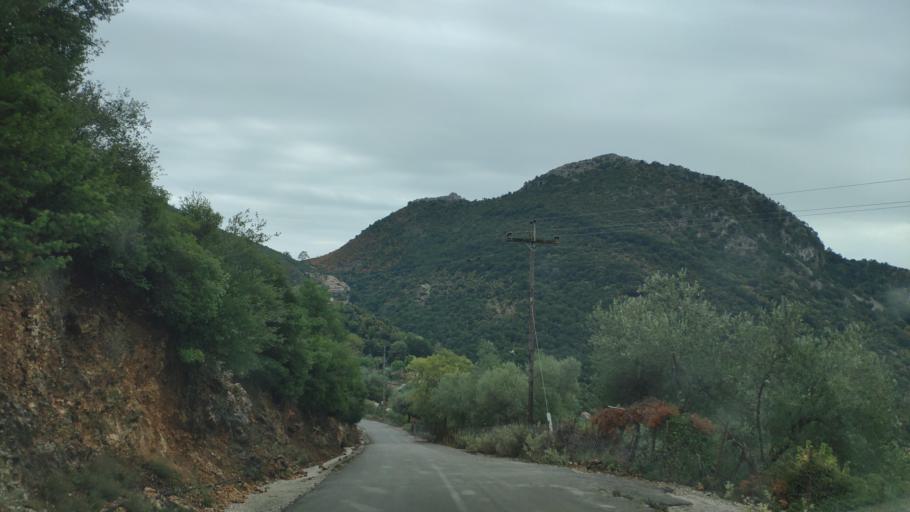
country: GR
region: Epirus
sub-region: Nomos Prevezis
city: Kanalaki
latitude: 39.3480
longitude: 20.6489
